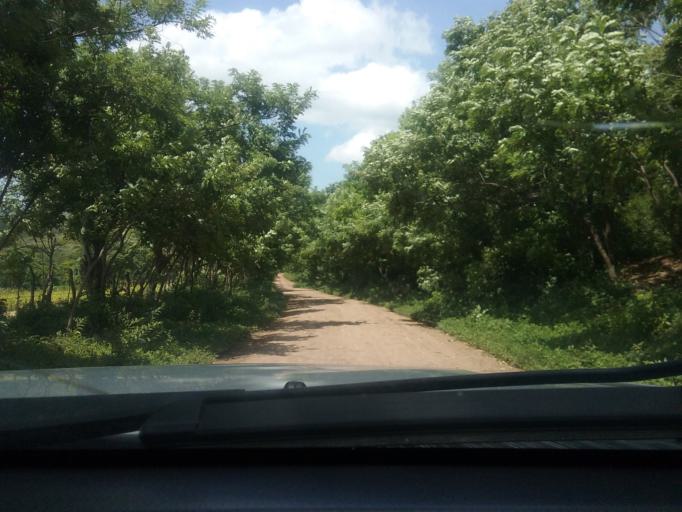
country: NI
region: Matagalpa
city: Terrabona
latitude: 12.6923
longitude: -85.9534
